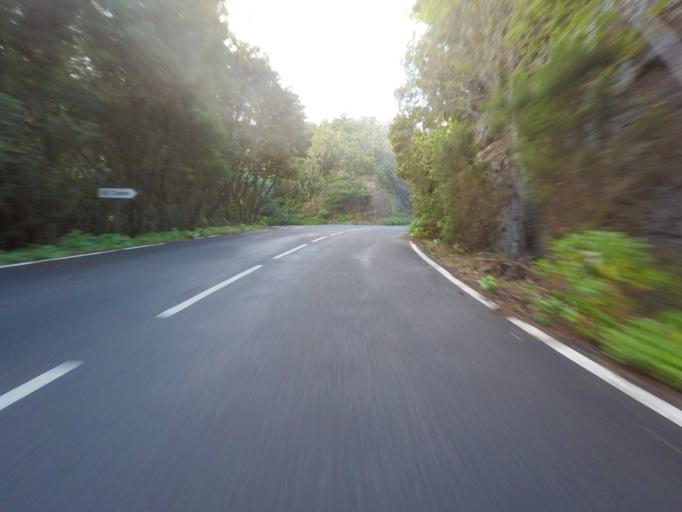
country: ES
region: Canary Islands
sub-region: Provincia de Santa Cruz de Tenerife
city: Hermigua
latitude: 28.1217
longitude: -17.2148
